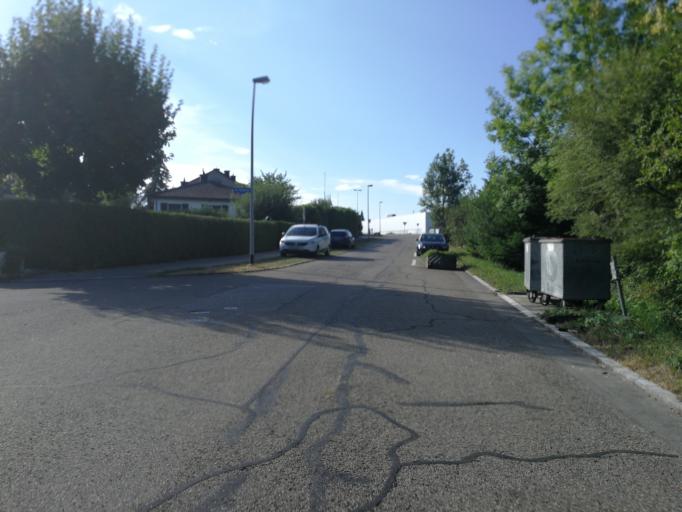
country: CH
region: Zurich
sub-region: Bezirk Meilen
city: Oetwil am See
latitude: 47.2769
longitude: 8.7230
